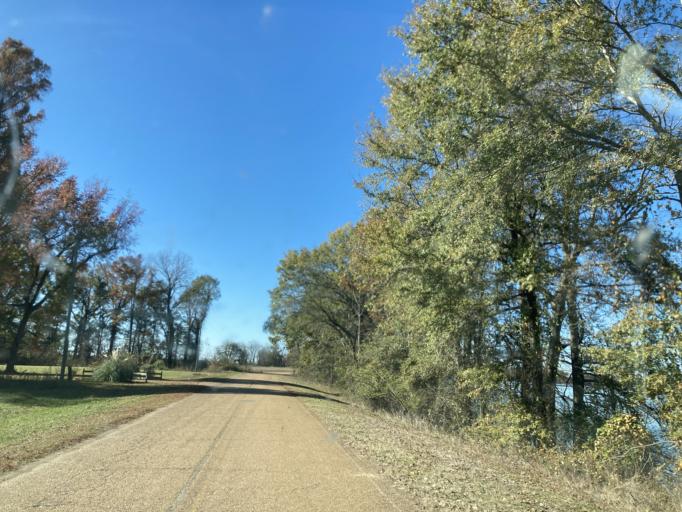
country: US
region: Mississippi
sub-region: Hinds County
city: Lynchburg
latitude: 32.6384
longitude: -90.6071
